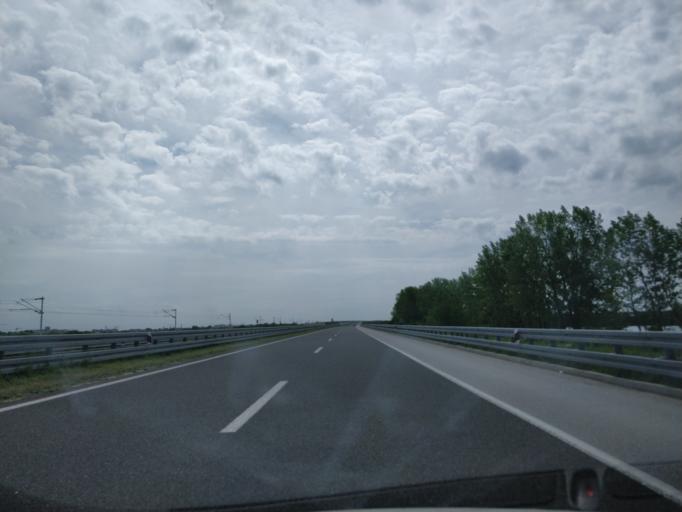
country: HR
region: Grad Zagreb
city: Odra
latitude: 45.7226
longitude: 16.0266
